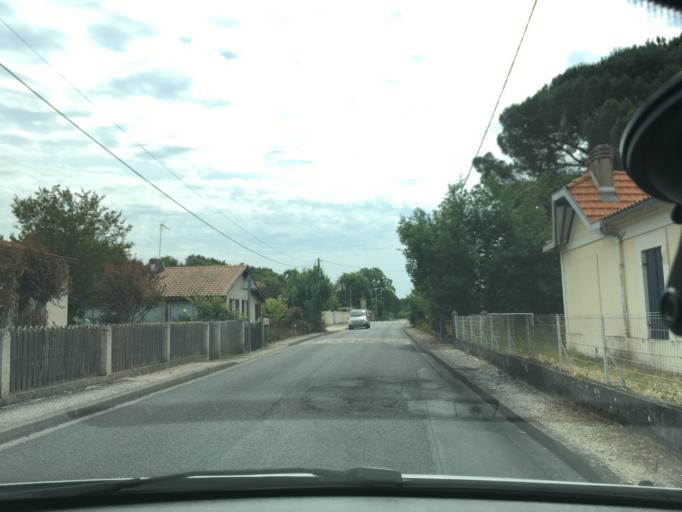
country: FR
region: Aquitaine
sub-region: Departement de la Gironde
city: Gaillan-en-Medoc
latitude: 45.3556
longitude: -1.0583
